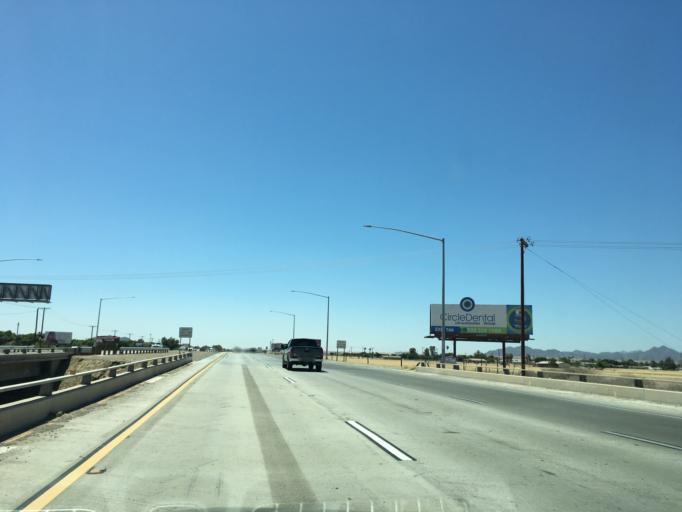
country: US
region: Arizona
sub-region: Yuma County
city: Yuma
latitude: 32.7326
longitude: -114.6272
